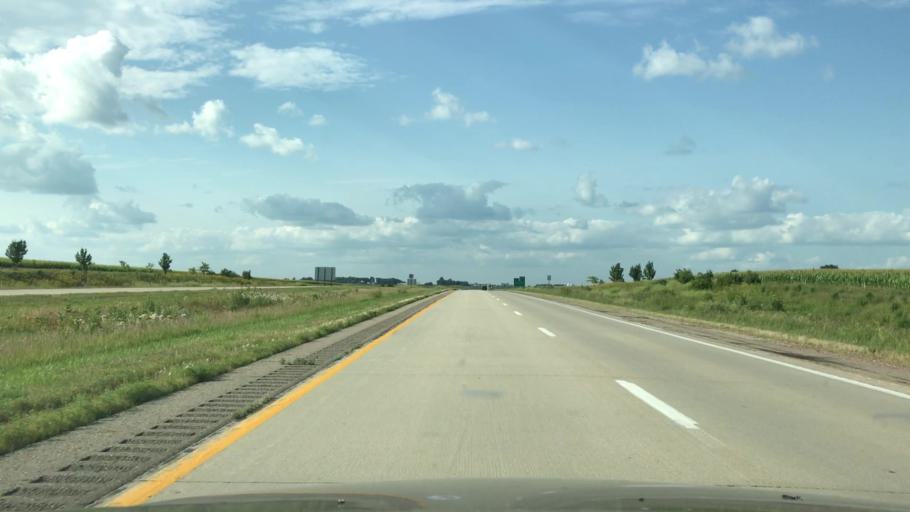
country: US
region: Iowa
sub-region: Osceola County
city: Sibley
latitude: 43.4129
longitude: -95.7170
